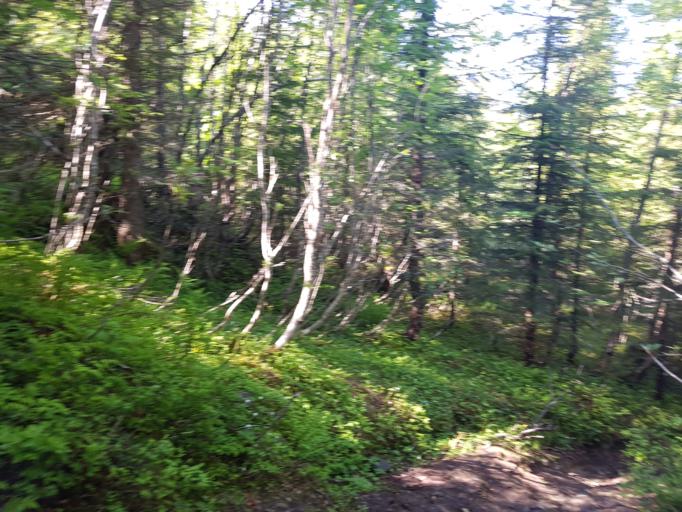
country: NO
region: Sor-Trondelag
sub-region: Trondheim
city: Trondheim
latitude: 63.4209
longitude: 10.2779
